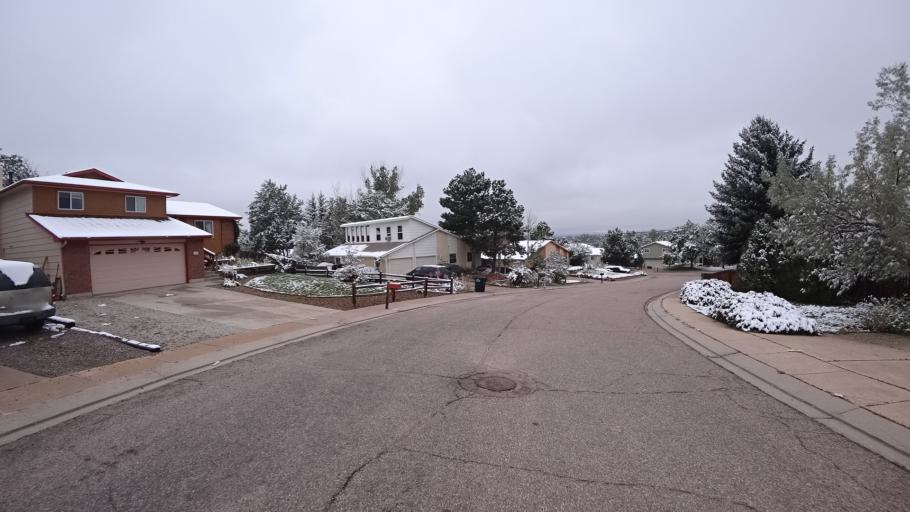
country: US
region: Colorado
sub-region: El Paso County
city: Cimarron Hills
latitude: 38.9228
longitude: -104.7725
